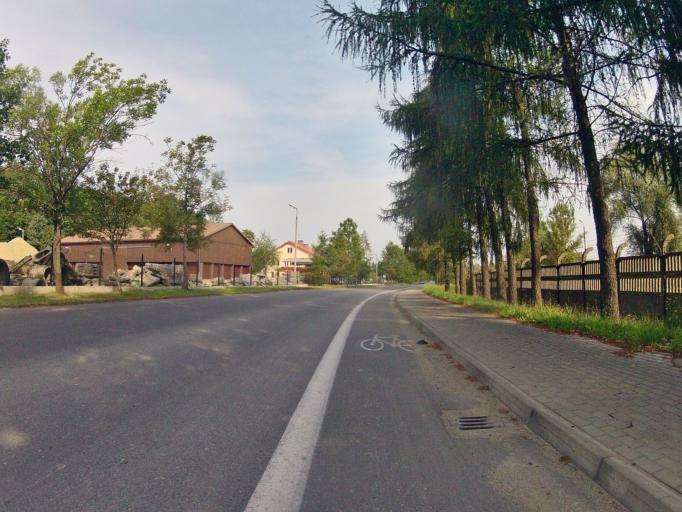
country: PL
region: Subcarpathian Voivodeship
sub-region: Powiat jasielski
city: Jaslo
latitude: 49.7214
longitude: 21.4509
